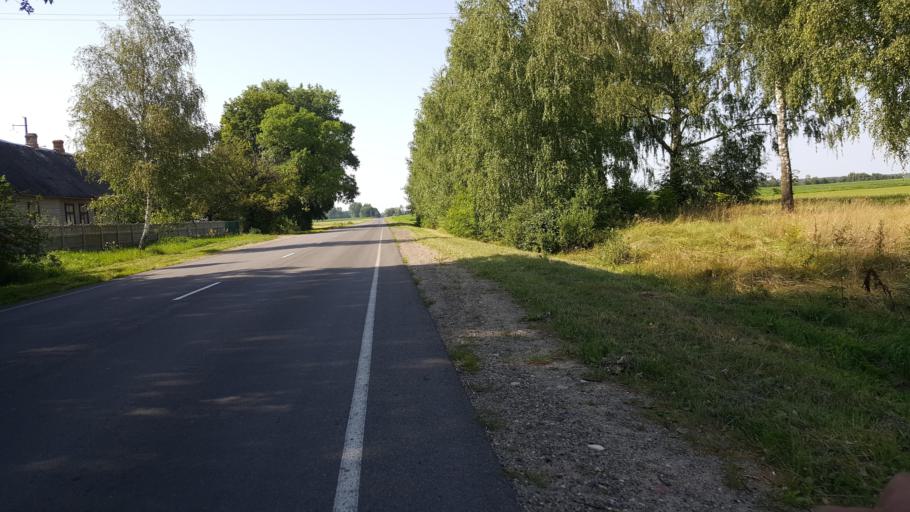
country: BY
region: Brest
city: Zhabinka
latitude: 52.2203
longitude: 23.9930
